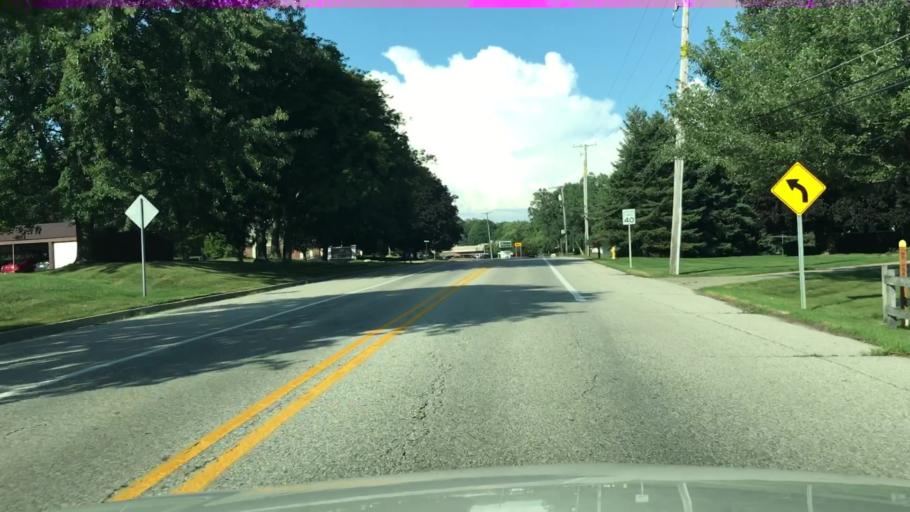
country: US
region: Michigan
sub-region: Macomb County
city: Clinton
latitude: 42.5803
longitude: -82.9456
